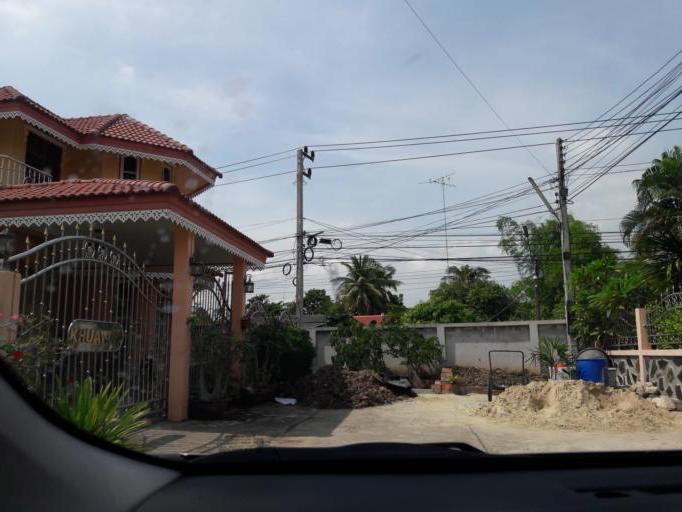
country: TH
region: Ang Thong
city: Ang Thong
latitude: 14.5780
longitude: 100.4425
